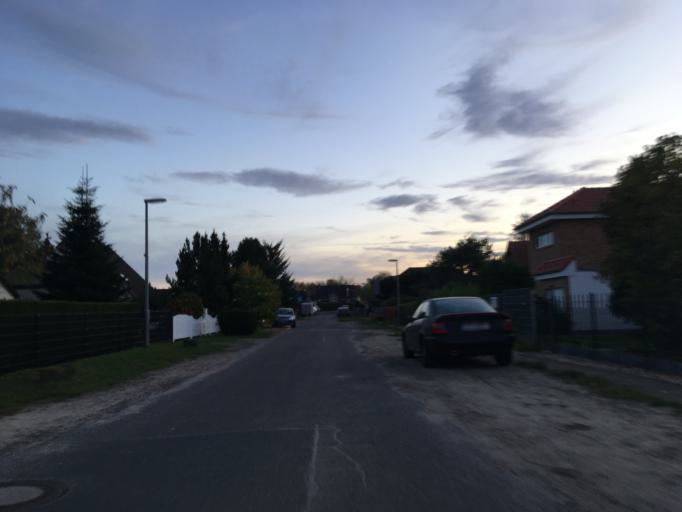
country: DE
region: Berlin
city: Buchholz
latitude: 52.6022
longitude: 13.4192
